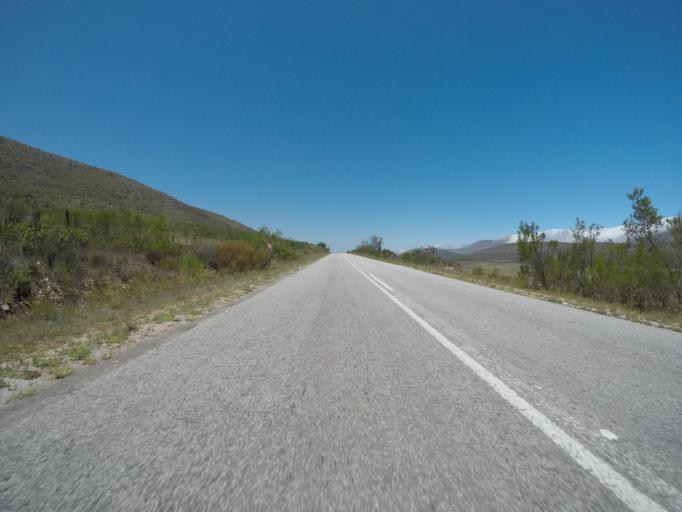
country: ZA
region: Eastern Cape
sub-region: Cacadu District Municipality
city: Kareedouw
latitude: -33.8381
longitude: 23.9234
